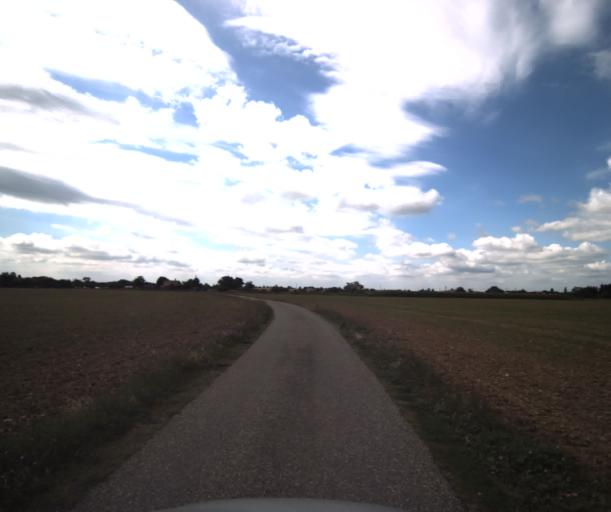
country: FR
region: Midi-Pyrenees
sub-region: Departement de la Haute-Garonne
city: Longages
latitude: 43.3708
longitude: 1.2443
